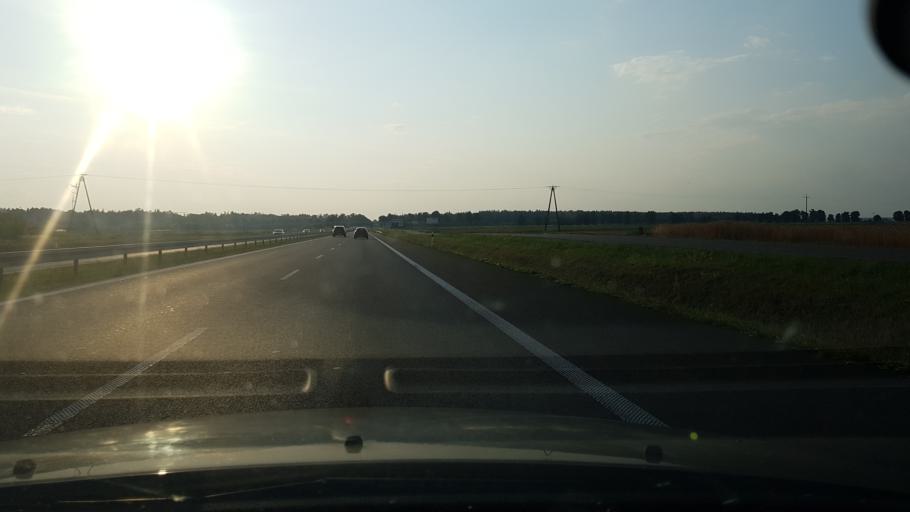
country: PL
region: Masovian Voivodeship
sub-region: Powiat nowodworski
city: Zakroczym
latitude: 52.4487
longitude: 20.5977
